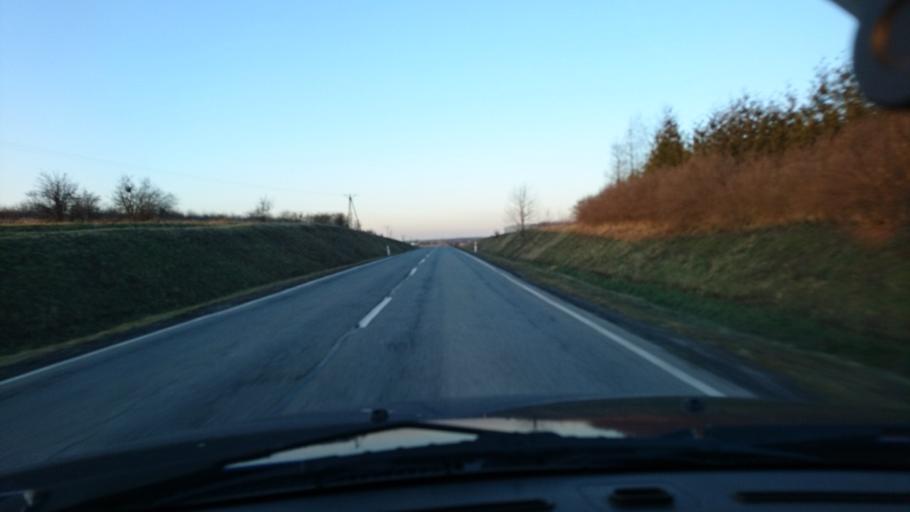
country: PL
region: Silesian Voivodeship
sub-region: Powiat gliwicki
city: Wielowies
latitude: 50.5070
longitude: 18.6046
